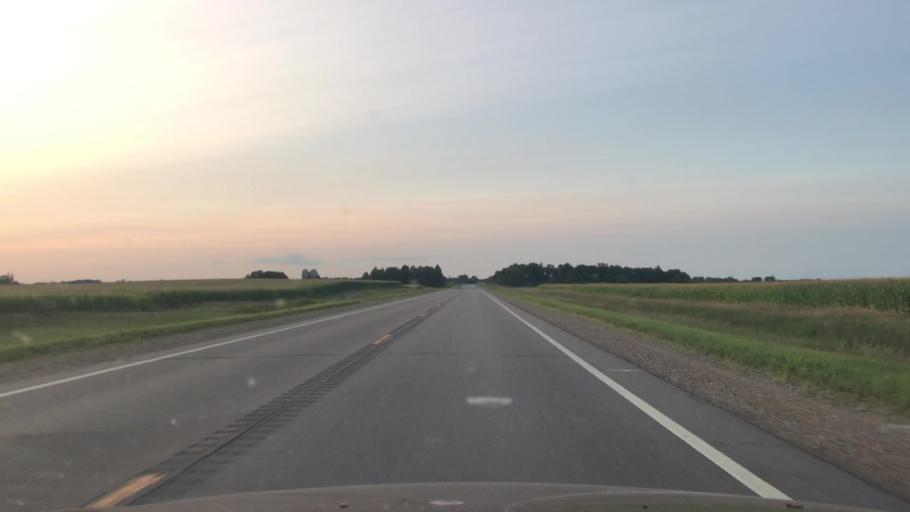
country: US
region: Minnesota
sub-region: Redwood County
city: Redwood Falls
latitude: 44.5115
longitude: -95.1180
